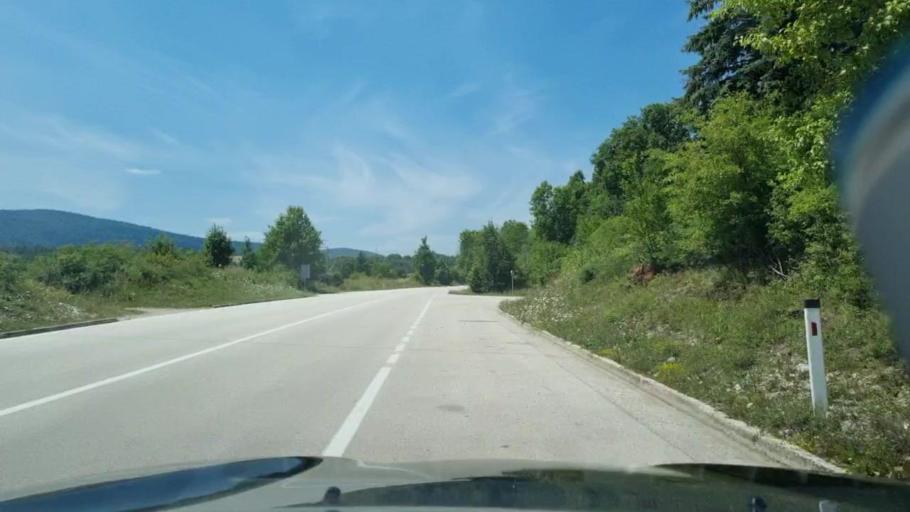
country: BA
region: Federation of Bosnia and Herzegovina
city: Sanica
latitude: 44.5489
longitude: 16.5787
